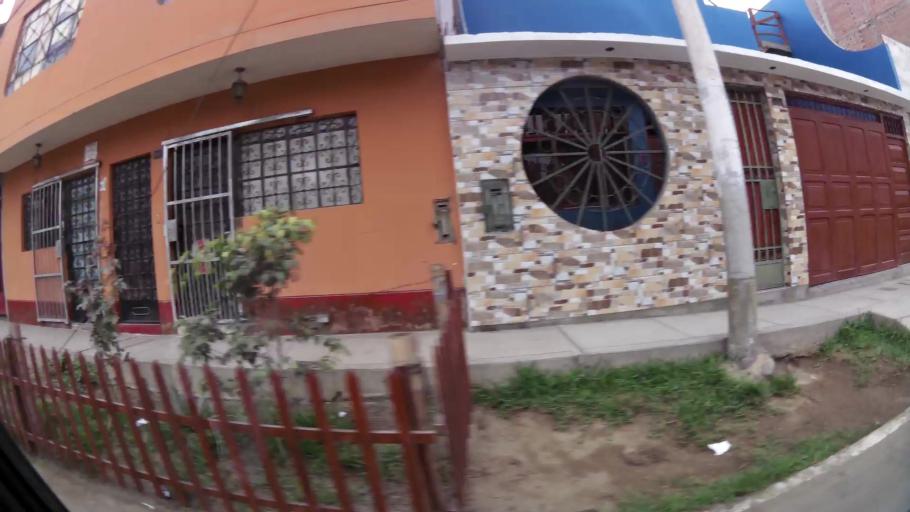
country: PE
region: Lima
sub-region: Lima
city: Urb. Santo Domingo
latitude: -11.8908
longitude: -77.0671
